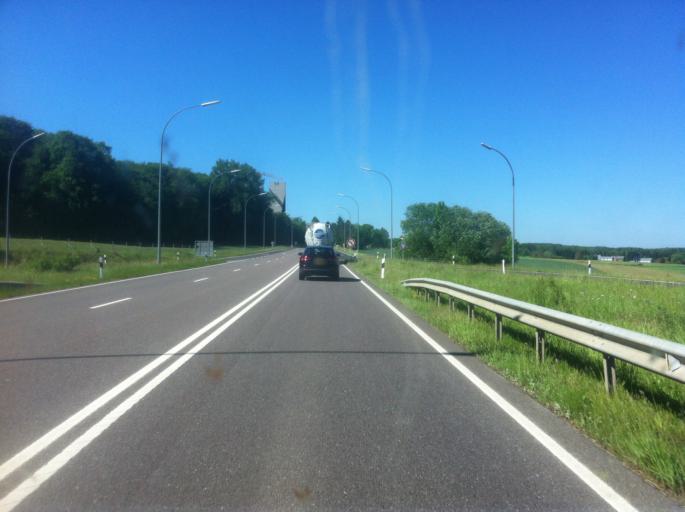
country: LU
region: Grevenmacher
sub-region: Canton d'Echternach
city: Consdorf
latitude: 49.7567
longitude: 6.3395
